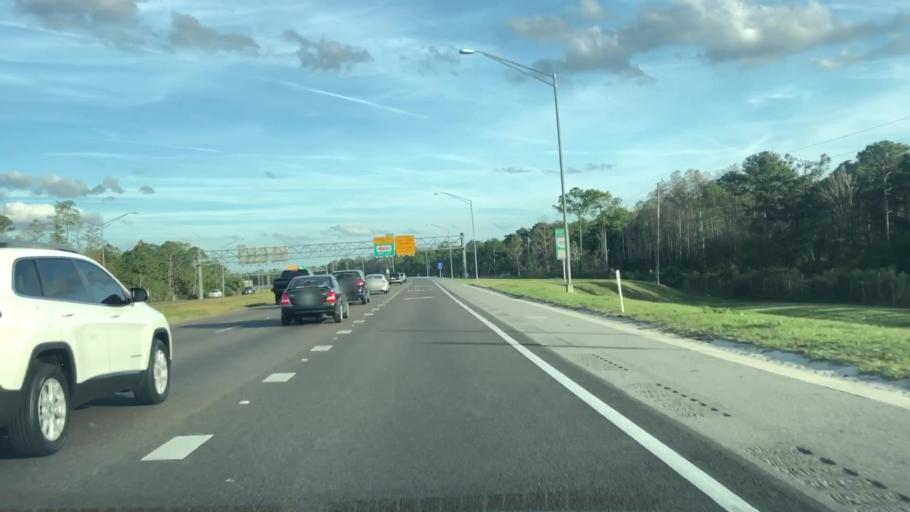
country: US
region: Florida
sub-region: Orange County
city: Hunters Creek
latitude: 28.3551
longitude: -81.4730
